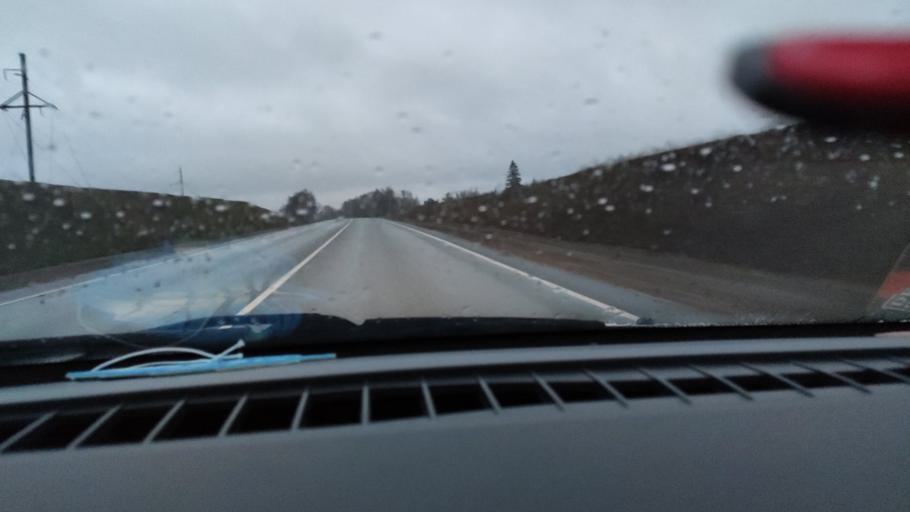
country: RU
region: Udmurtiya
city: Alnashi
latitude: 56.2229
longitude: 52.4162
